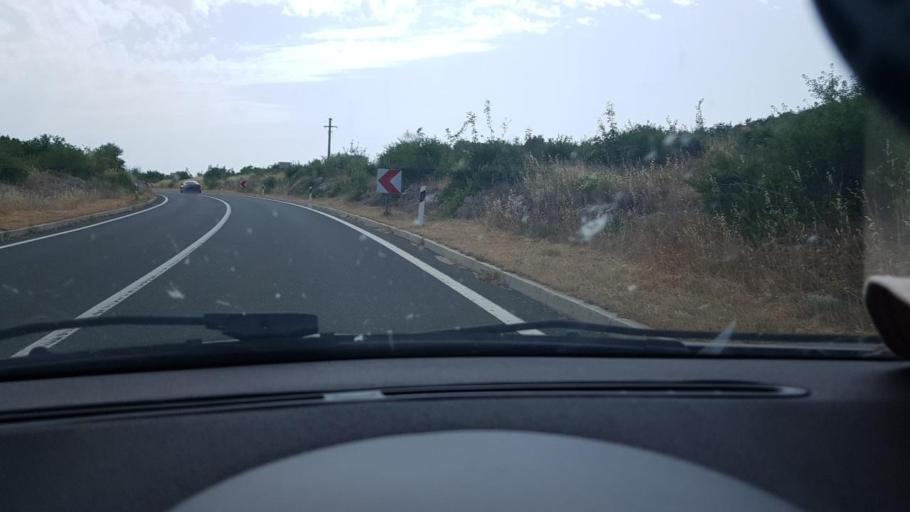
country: HR
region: Sibensko-Kniniska
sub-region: Grad Sibenik
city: Pirovac
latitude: 43.8776
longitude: 15.7427
